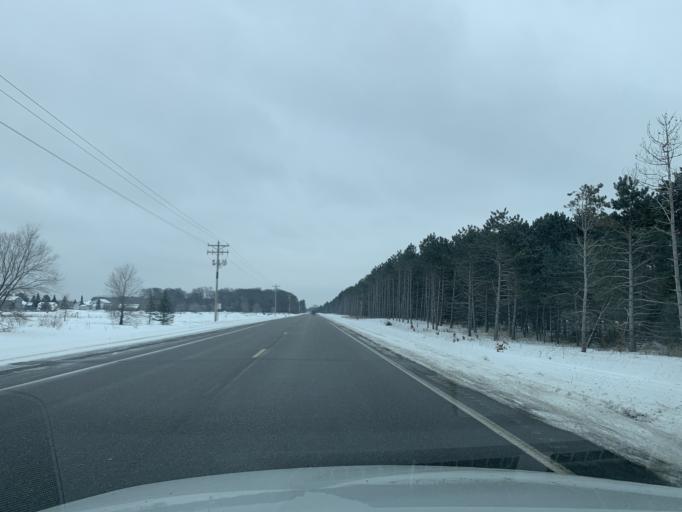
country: US
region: Minnesota
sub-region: Sherburne County
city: Zimmerman
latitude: 45.5013
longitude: -93.6286
